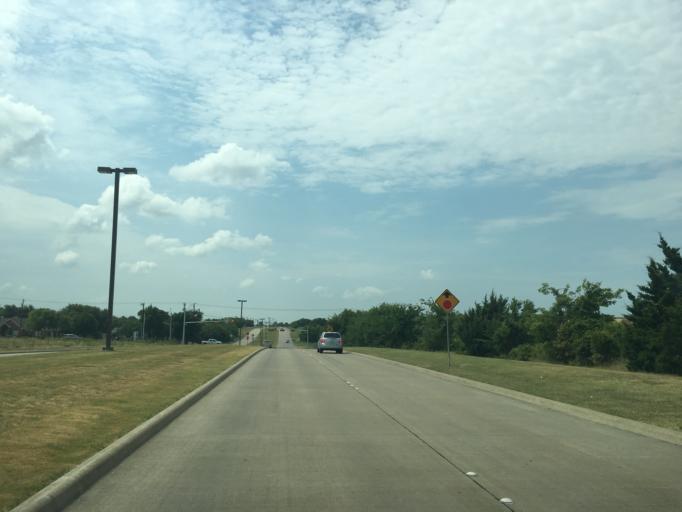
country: US
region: Texas
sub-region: Rockwall County
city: Rockwall
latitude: 32.9673
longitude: -96.4526
